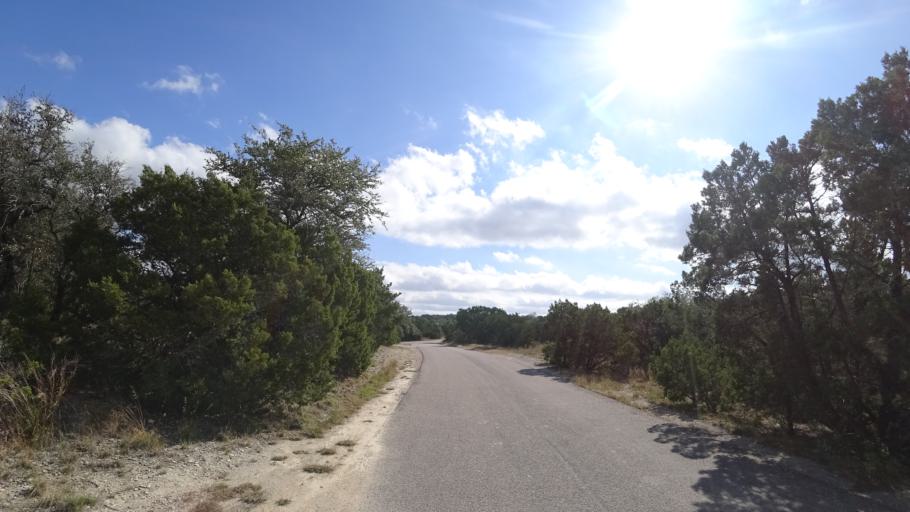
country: US
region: Texas
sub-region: Travis County
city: Bee Cave
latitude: 30.2592
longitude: -97.9385
